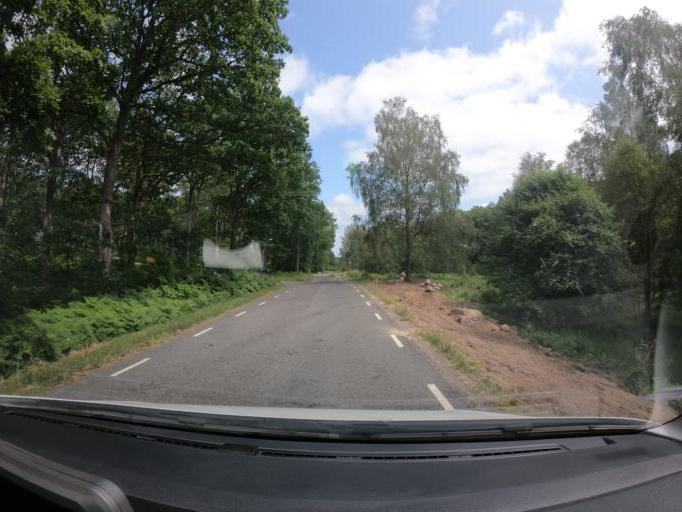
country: SE
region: Skane
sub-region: Hassleholms Kommun
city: Sosdala
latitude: 56.0543
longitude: 13.6188
